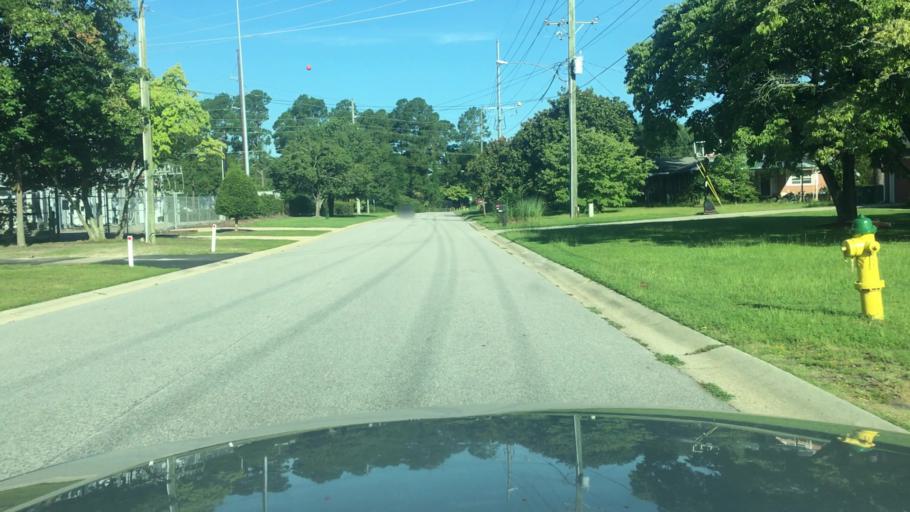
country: US
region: North Carolina
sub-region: Cumberland County
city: Fayetteville
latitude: 35.1313
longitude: -78.8910
